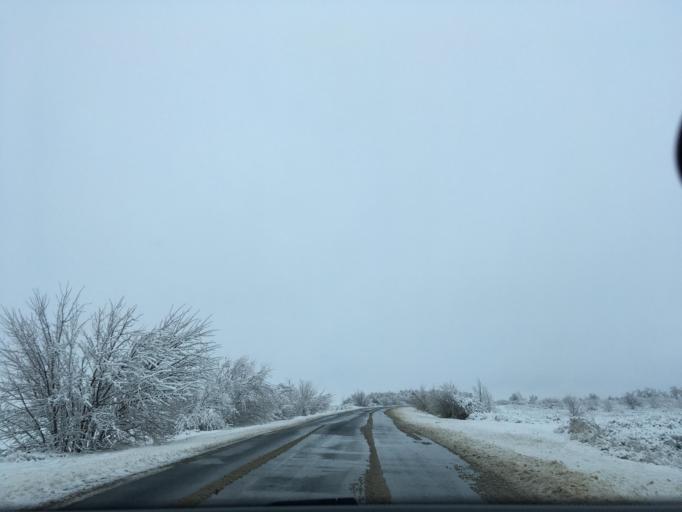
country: RU
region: Voronezj
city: Ol'khovatka
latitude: 50.1247
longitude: 39.1773
